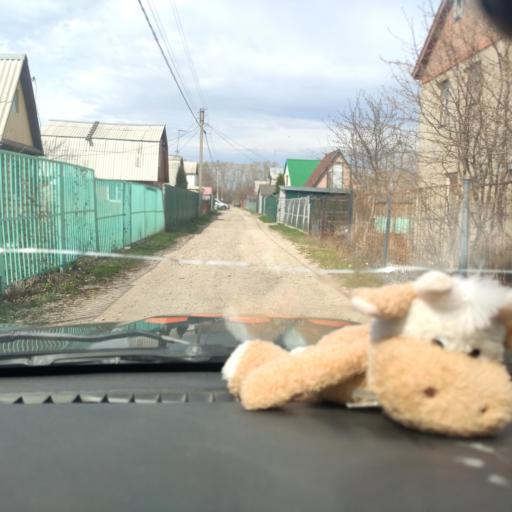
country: RU
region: Samara
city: Tol'yatti
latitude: 53.6028
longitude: 49.2414
